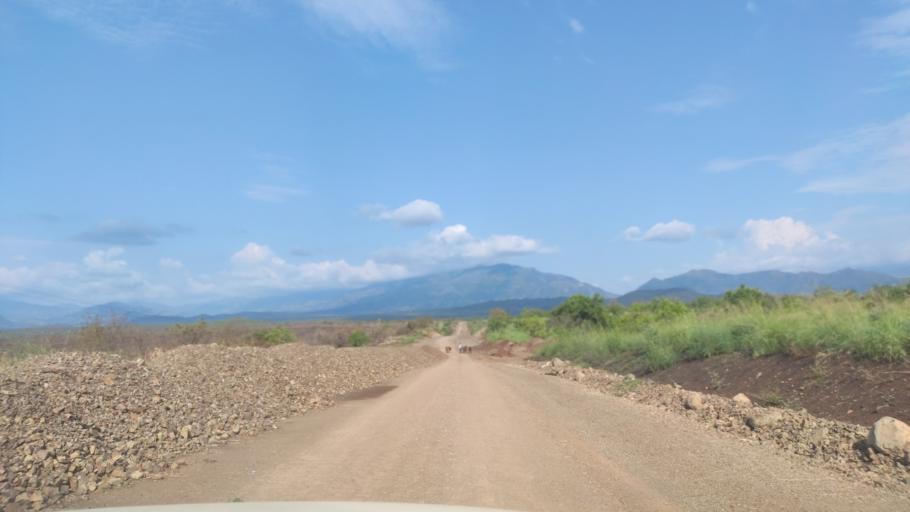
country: ET
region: Southern Nations, Nationalities, and People's Region
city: Felege Neway
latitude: 6.4250
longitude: 37.2475
